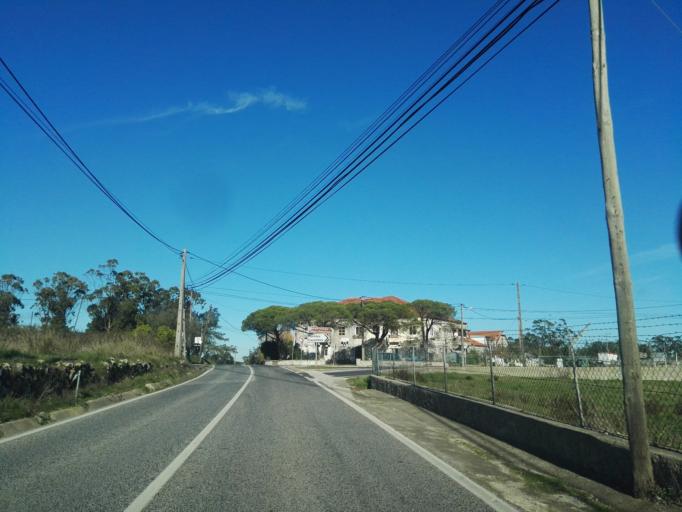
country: PT
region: Lisbon
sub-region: Mafra
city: Milharado
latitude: 38.8964
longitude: -9.1866
